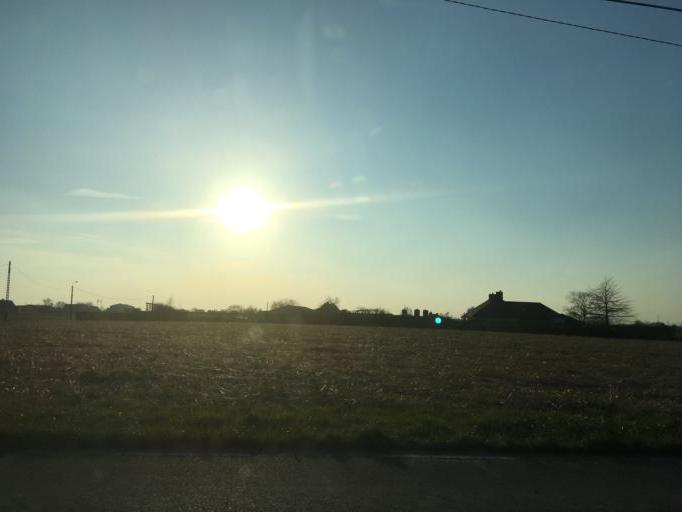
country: BE
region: Flanders
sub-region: Provincie West-Vlaanderen
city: Meulebeke
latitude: 50.9703
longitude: 3.2756
